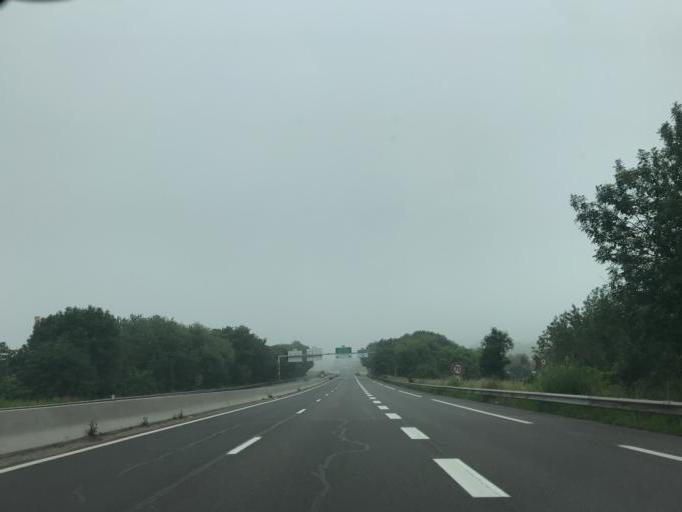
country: FR
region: Ile-de-France
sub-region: Departement de Seine-et-Marne
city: Saint-Thibault-des-Vignes
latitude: 48.8669
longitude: 2.6750
